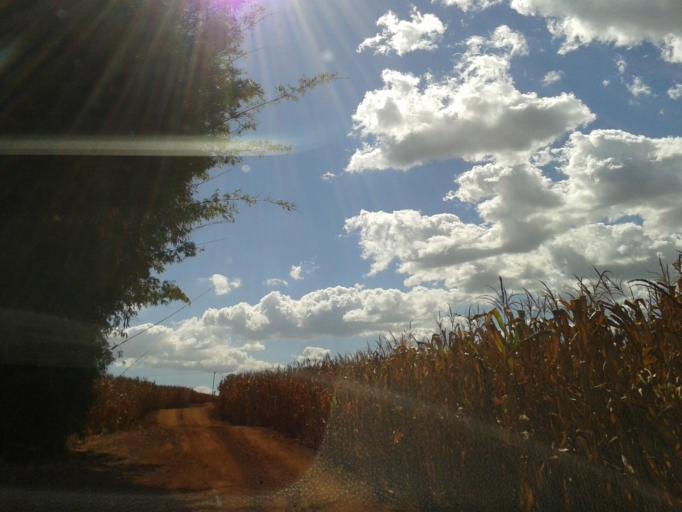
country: BR
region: Minas Gerais
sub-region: Capinopolis
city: Capinopolis
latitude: -18.6268
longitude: -49.4727
